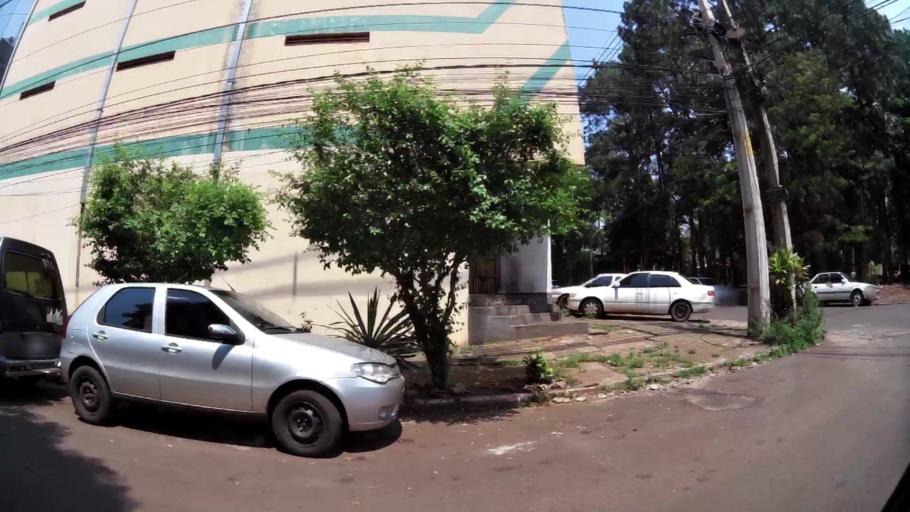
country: PY
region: Alto Parana
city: Ciudad del Este
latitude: -25.5164
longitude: -54.6112
